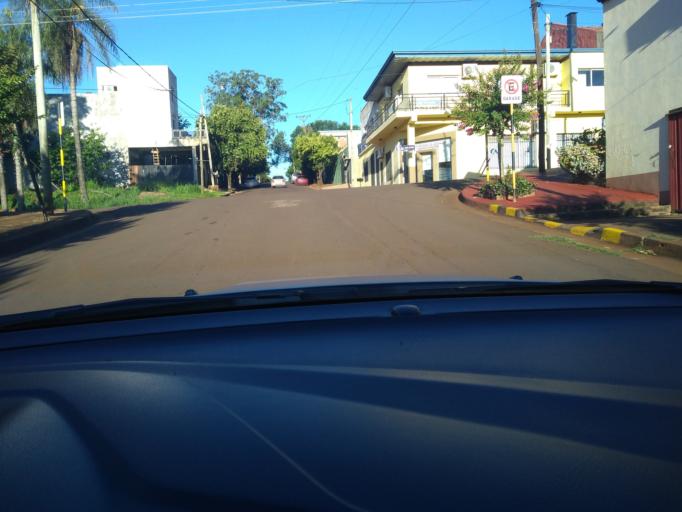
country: AR
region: Misiones
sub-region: Departamento de Obera
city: Obera
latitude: -27.4818
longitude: -55.1155
